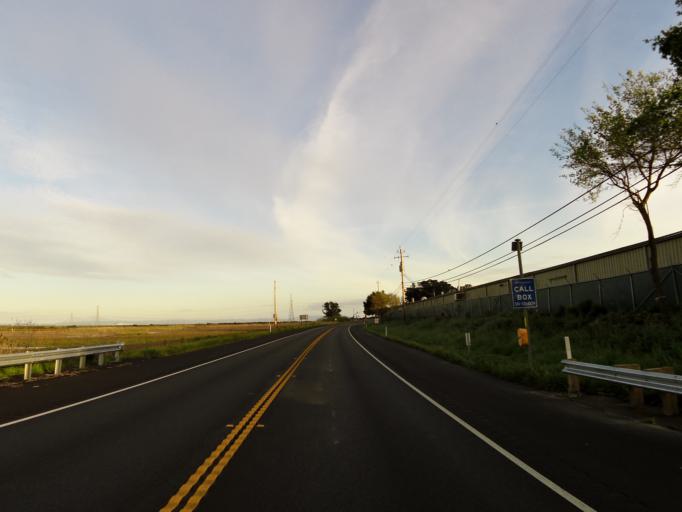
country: US
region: California
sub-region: Marin County
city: Black Point-Green Point
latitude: 38.1610
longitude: -122.4521
